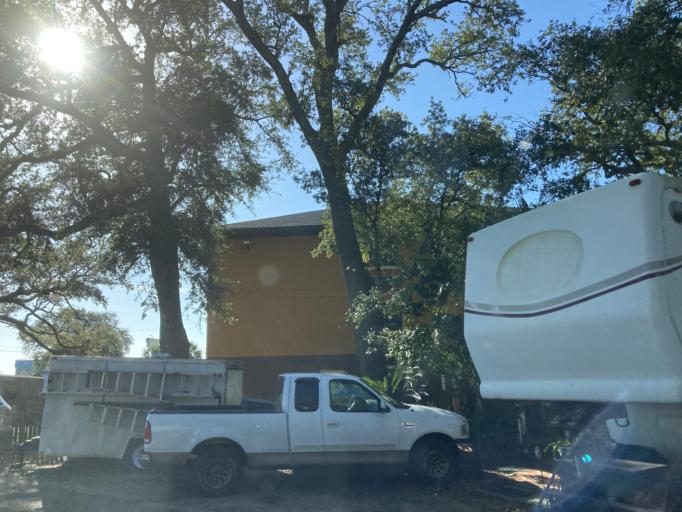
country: US
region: Mississippi
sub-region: Harrison County
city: Biloxi
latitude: 30.3948
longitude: -88.9434
